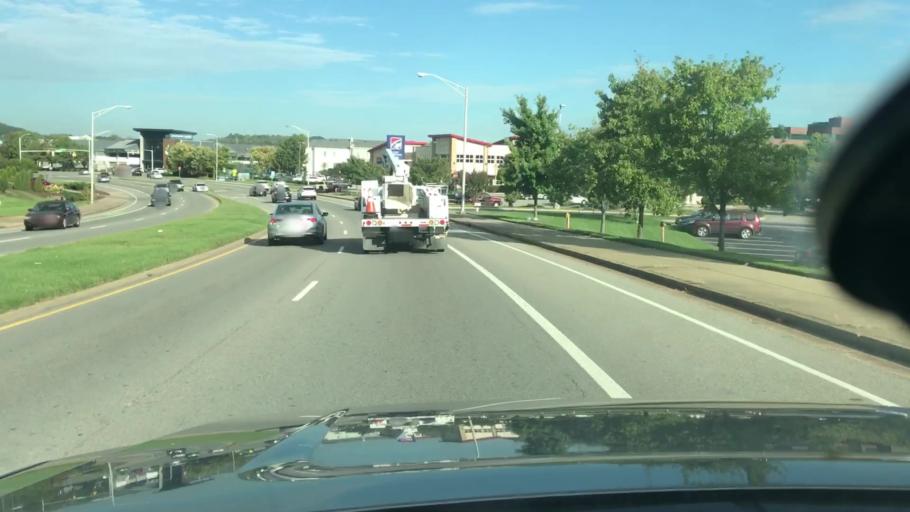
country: US
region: Tennessee
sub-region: Davidson County
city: Nashville
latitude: 36.1917
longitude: -86.7992
